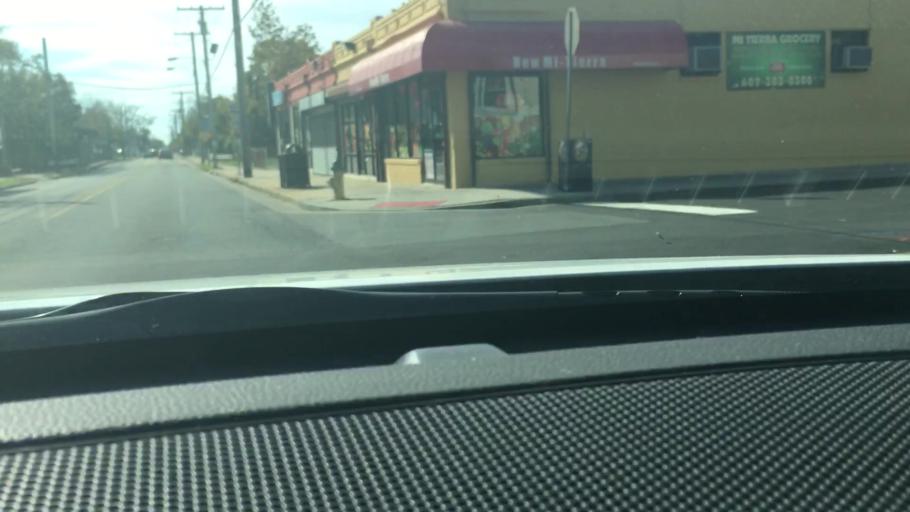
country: US
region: New Jersey
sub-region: Atlantic County
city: Pleasantville
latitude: 39.3991
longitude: -74.5161
